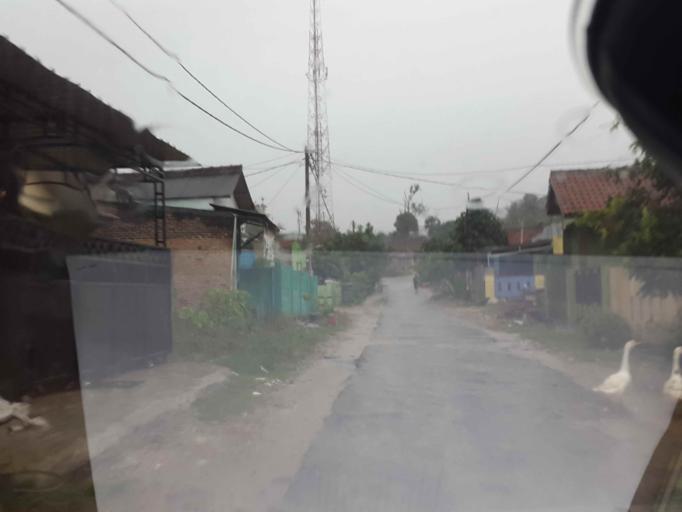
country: ID
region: Lampung
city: Panjang
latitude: -5.4018
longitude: 105.3513
